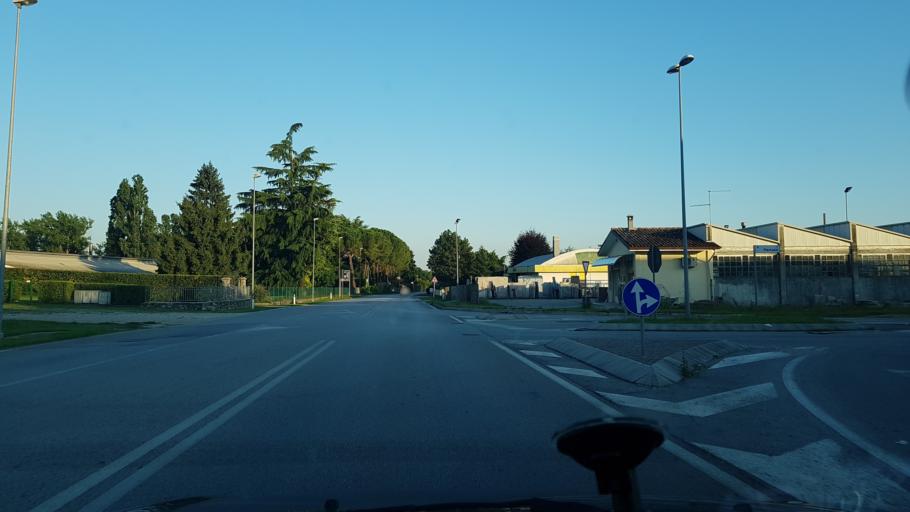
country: IT
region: Friuli Venezia Giulia
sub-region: Provincia di Udine
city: Fagagna
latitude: 46.1032
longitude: 13.0945
